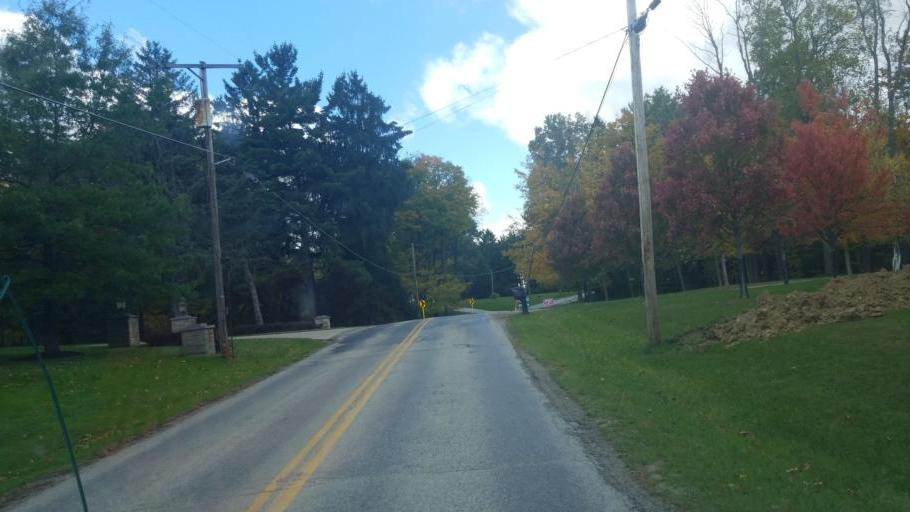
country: US
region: Ohio
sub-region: Richland County
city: Ontario
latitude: 40.7338
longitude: -82.5793
